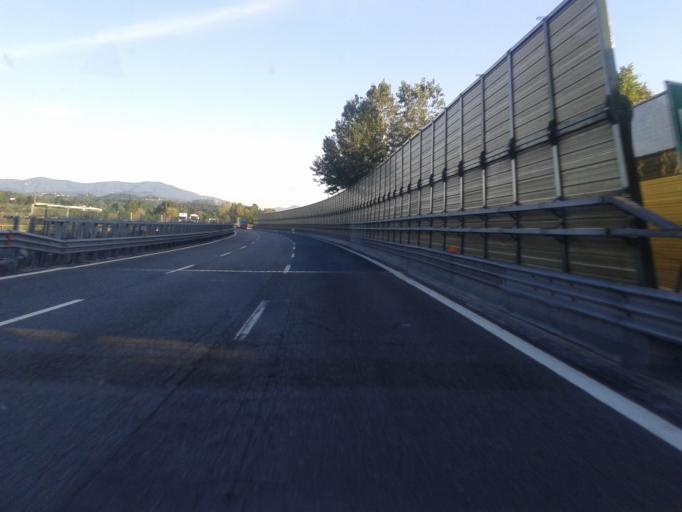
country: IT
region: Piedmont
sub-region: Provincia di Alessandria
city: Rocca Grimalda
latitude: 44.6760
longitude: 8.6580
